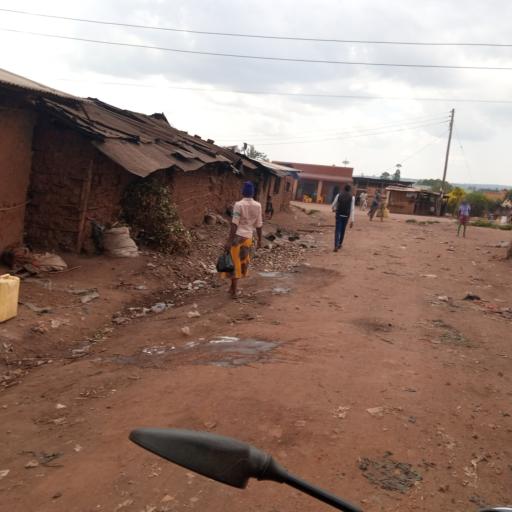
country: UG
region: Eastern Region
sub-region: Mbale District
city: Mbale
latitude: 1.0980
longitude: 34.1772
